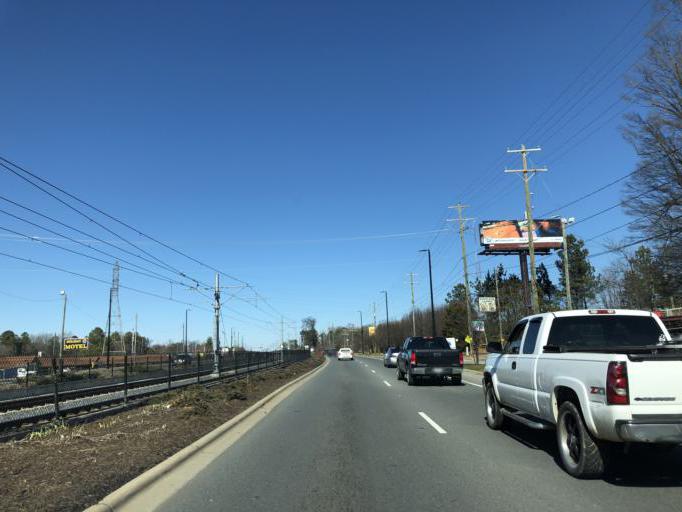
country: US
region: North Carolina
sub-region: Mecklenburg County
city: Charlotte
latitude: 35.2668
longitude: -80.7686
